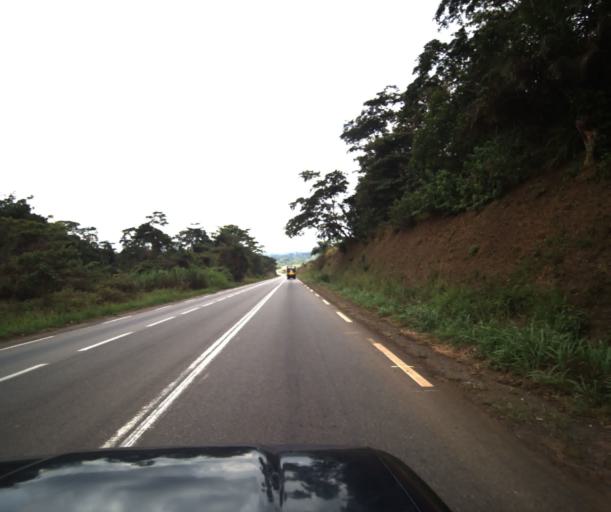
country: CM
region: Centre
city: Eseka
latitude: 3.8536
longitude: 10.9617
